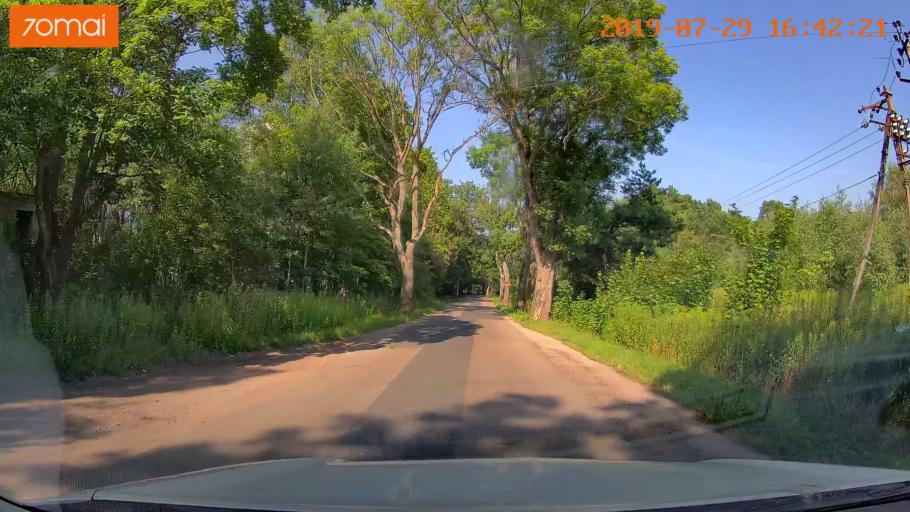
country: RU
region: Kaliningrad
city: Primorsk
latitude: 54.7423
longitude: 20.0722
